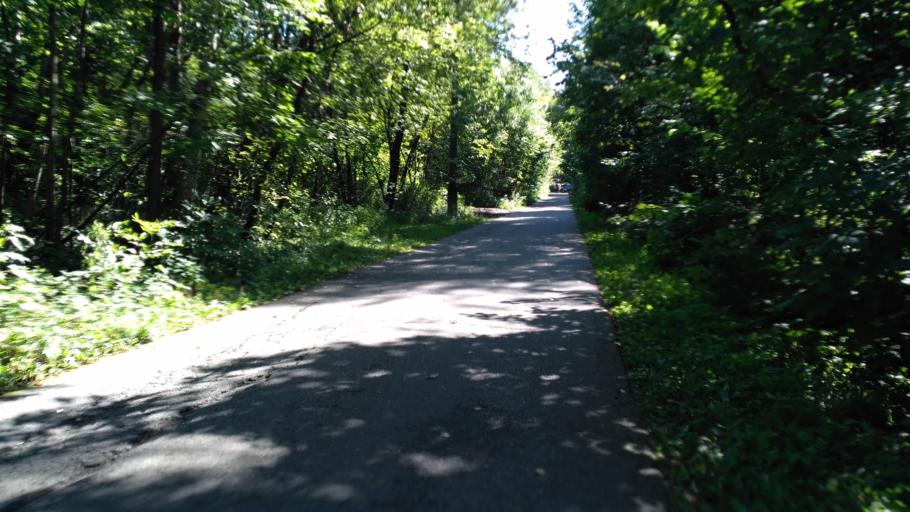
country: RU
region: Moscow
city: Metrogorodok
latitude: 55.7783
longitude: 37.7590
